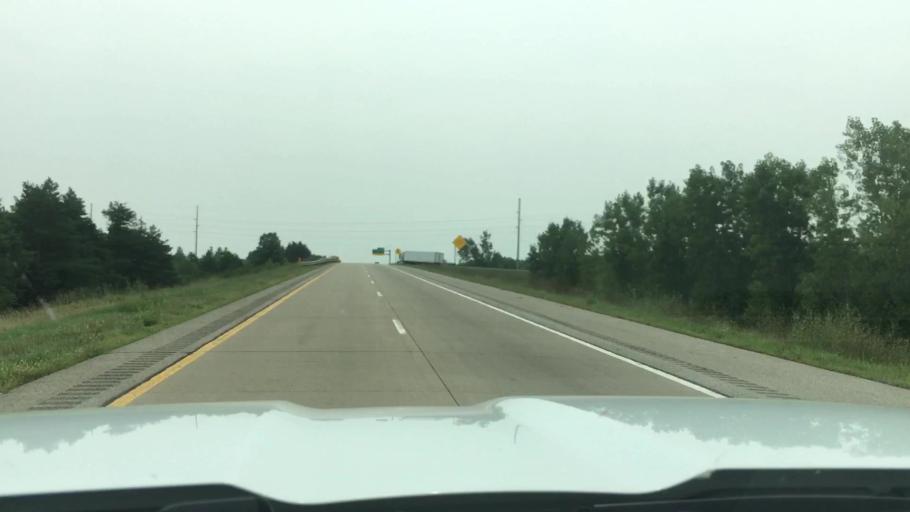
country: US
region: Michigan
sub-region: Eaton County
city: Dimondale
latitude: 42.6788
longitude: -84.6561
